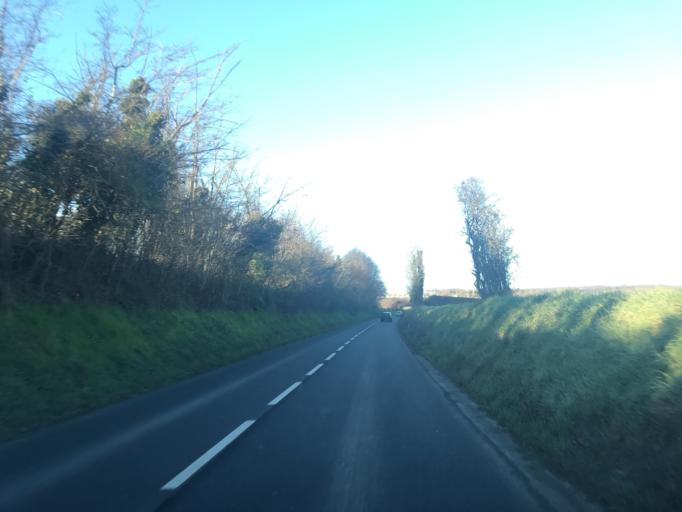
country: FR
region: Lower Normandy
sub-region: Departement du Calvados
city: Beuville
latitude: 49.2197
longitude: -0.3386
